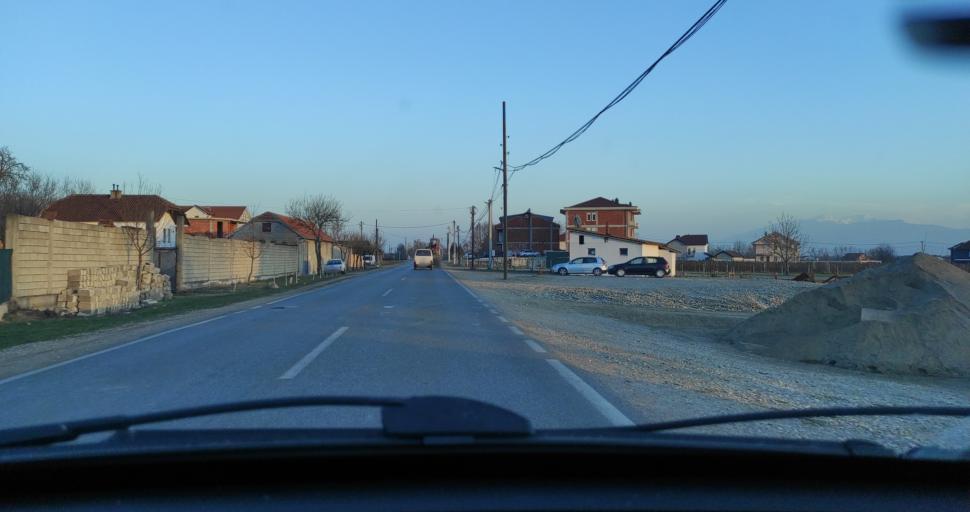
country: XK
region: Gjakova
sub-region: Komuna e Decanit
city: Gllogjan
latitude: 42.4348
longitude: 20.3758
